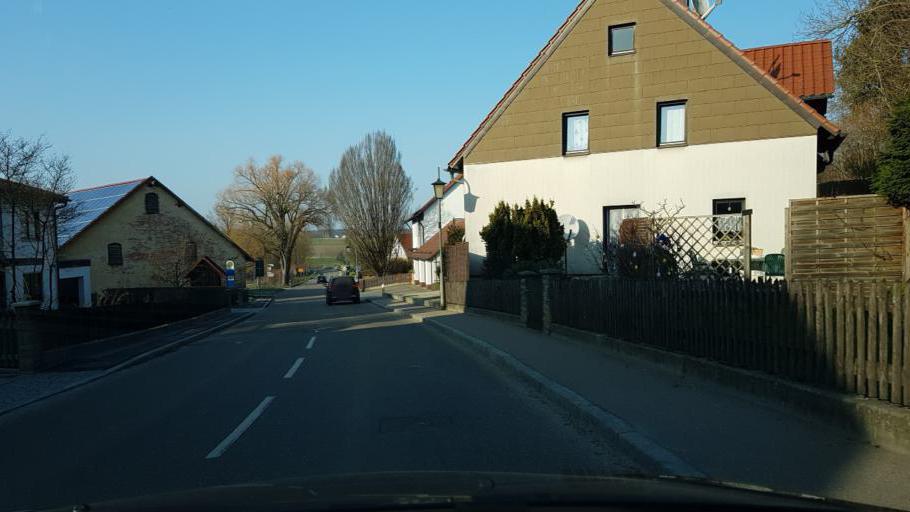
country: DE
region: Bavaria
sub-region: Upper Bavaria
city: Odelzhausen
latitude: 48.3144
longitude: 11.2043
